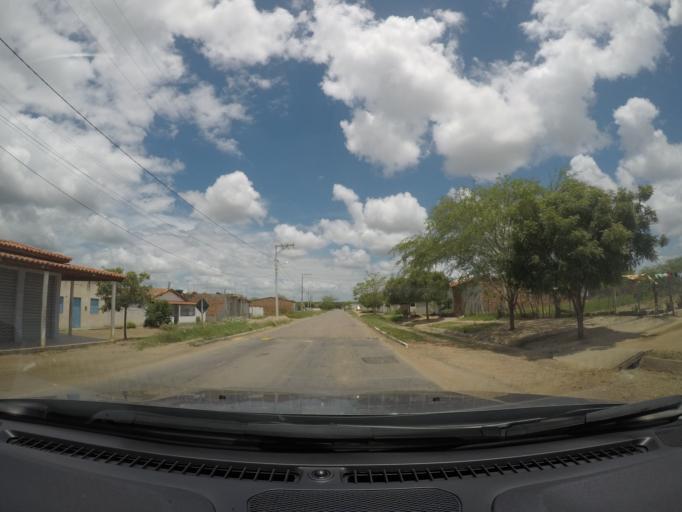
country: BR
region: Bahia
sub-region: Itaberaba
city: Itaberaba
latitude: -12.3629
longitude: -40.0436
